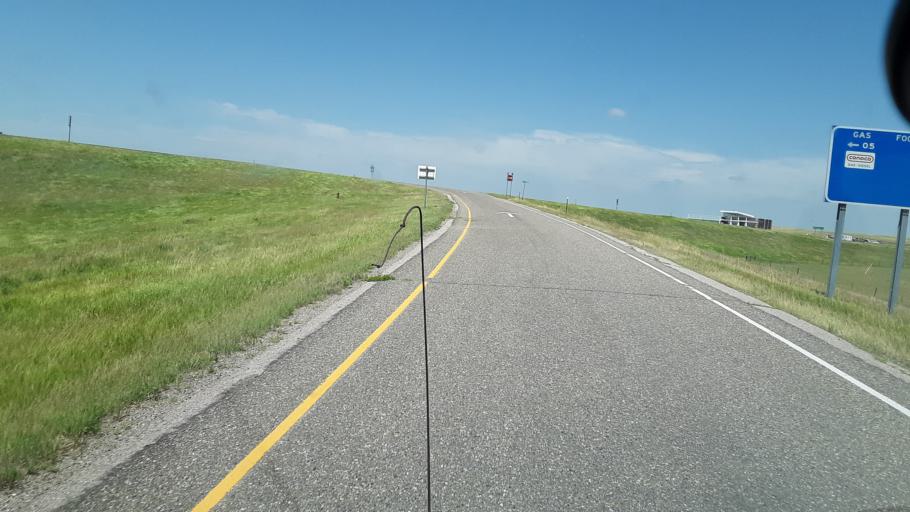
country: US
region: South Dakota
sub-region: Haakon County
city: Philip
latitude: 43.8410
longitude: -101.8981
